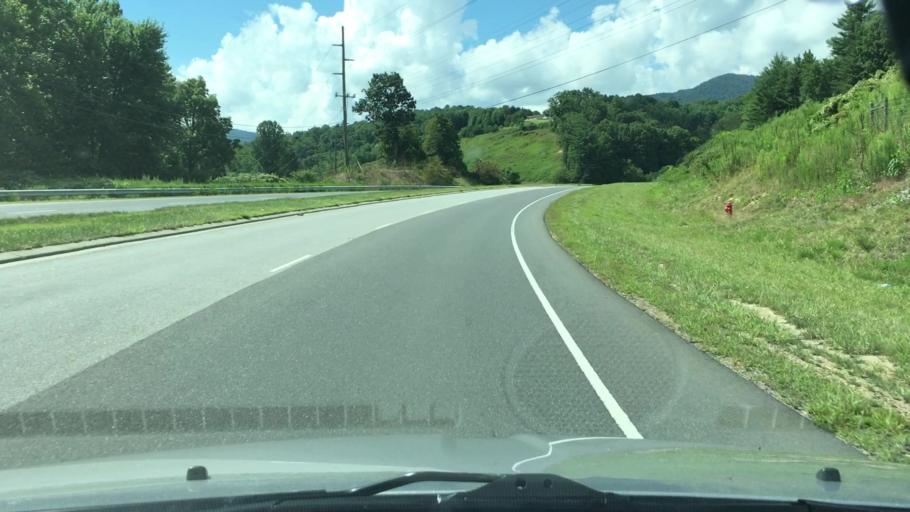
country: US
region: North Carolina
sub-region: Yancey County
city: Burnsville
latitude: 35.9125
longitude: -82.2355
